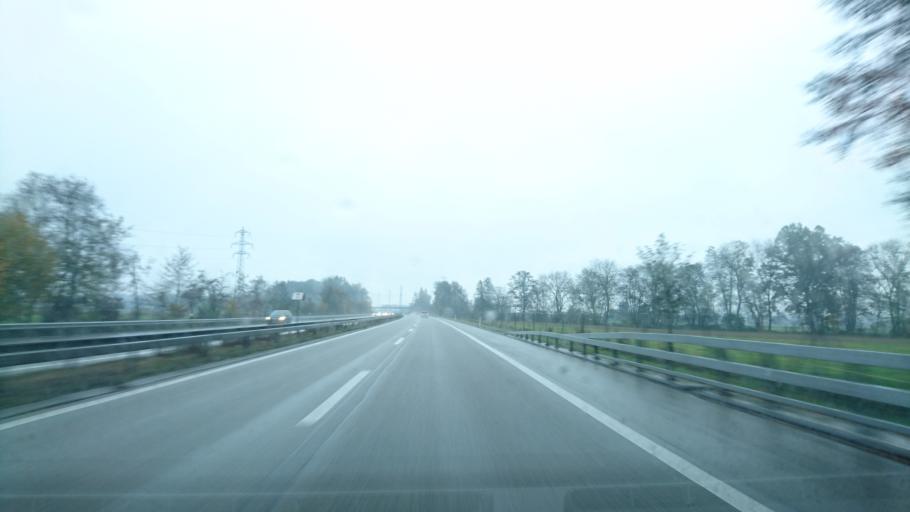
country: CH
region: Solothurn
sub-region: Bezirk Wasseramt
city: Kriegstetten
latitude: 47.1869
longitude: 7.5973
